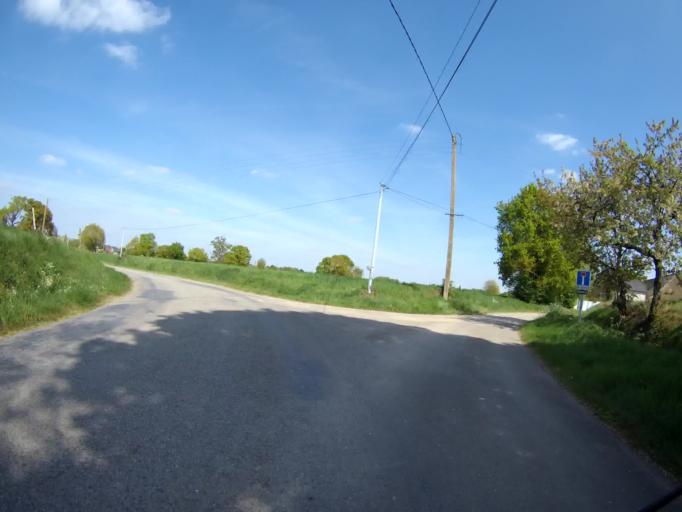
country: FR
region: Brittany
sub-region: Departement d'Ille-et-Vilaine
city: Vern-sur-Seiche
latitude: 48.0326
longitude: -1.6208
